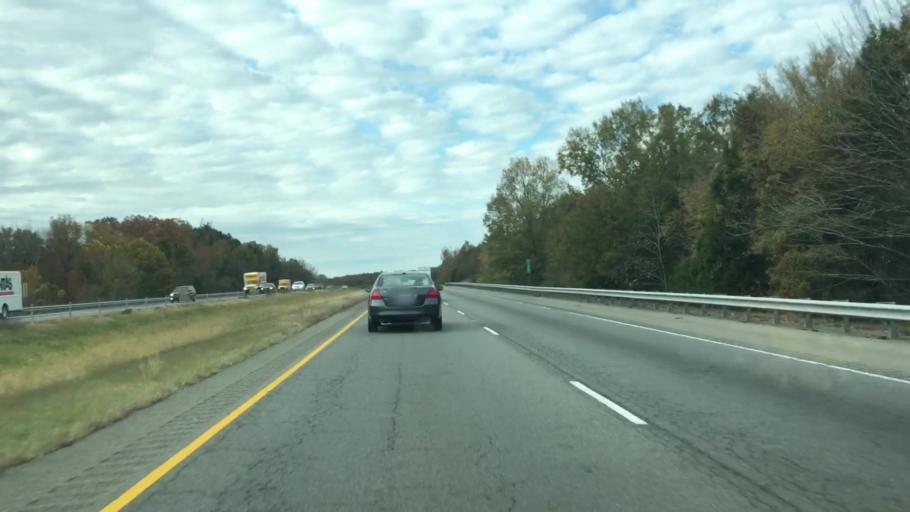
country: US
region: Arkansas
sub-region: Faulkner County
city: Conway
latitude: 35.1332
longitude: -92.5172
